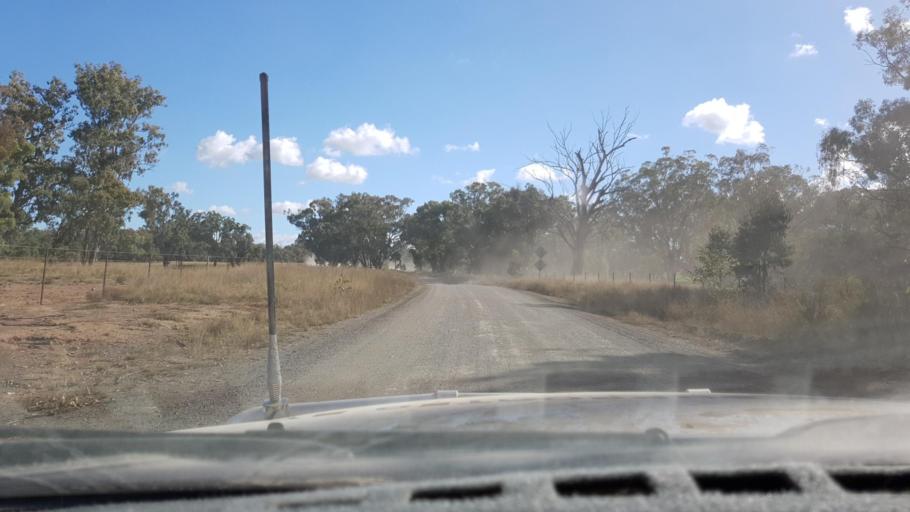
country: AU
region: New South Wales
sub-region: Tamworth Municipality
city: Manilla
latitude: -30.5988
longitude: 150.4975
